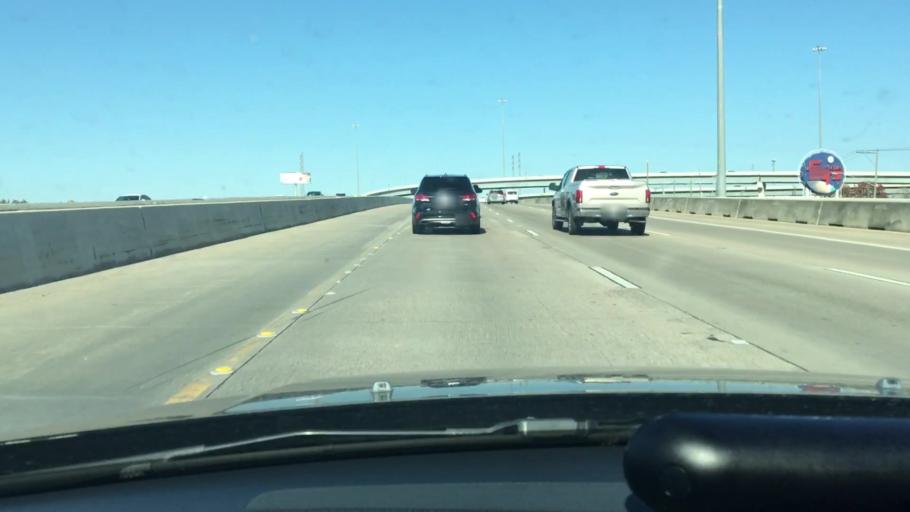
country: US
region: Texas
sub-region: Harris County
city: Webster
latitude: 29.5194
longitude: -95.1235
